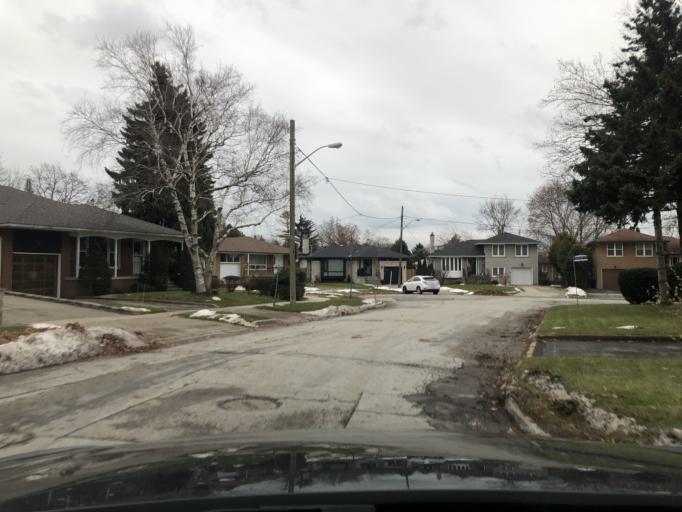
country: CA
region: Ontario
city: Etobicoke
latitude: 43.6907
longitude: -79.5242
